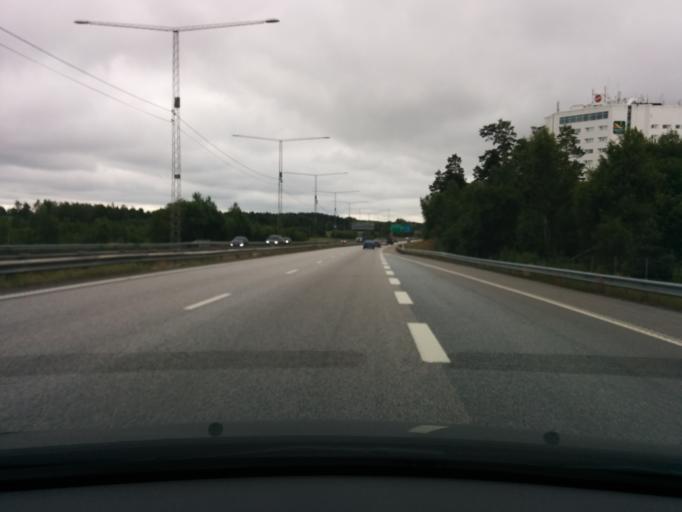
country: SE
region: Stockholm
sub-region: Sigtuna Kommun
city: Rosersberg
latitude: 59.6094
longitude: 17.8993
